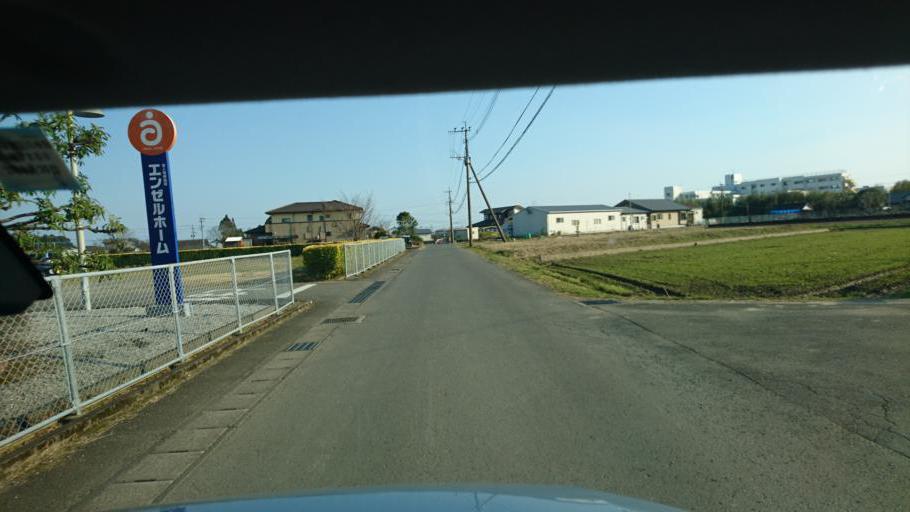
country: JP
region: Miyazaki
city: Miyazaki-shi
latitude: 32.0047
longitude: 131.4401
